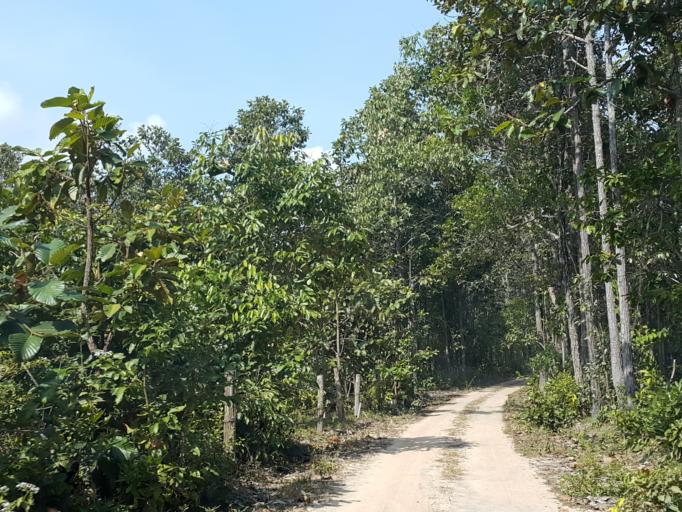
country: TH
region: Chiang Mai
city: Hot
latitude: 18.1251
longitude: 98.4380
